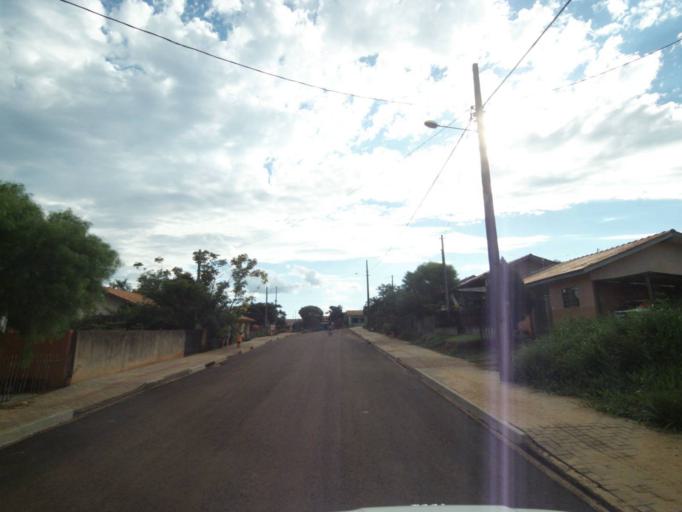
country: BR
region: Parana
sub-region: Laranjeiras Do Sul
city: Laranjeiras do Sul
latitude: -25.4954
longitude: -52.5245
